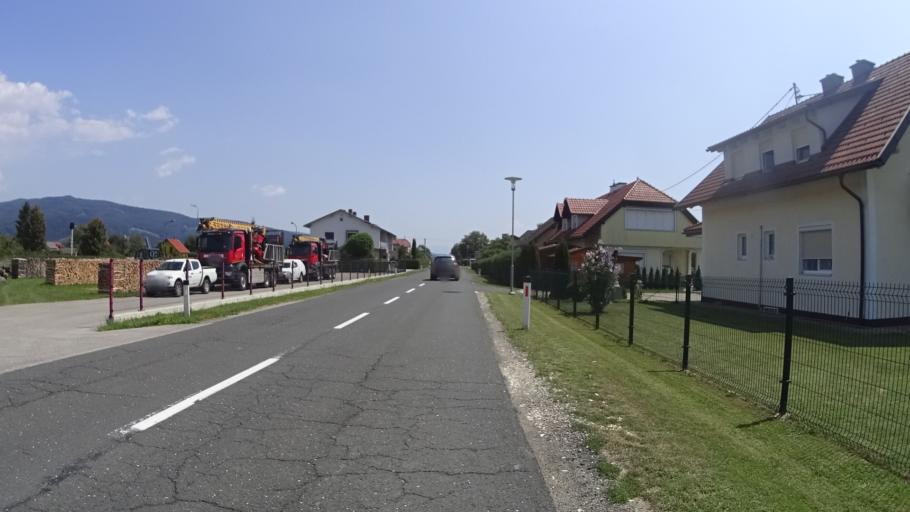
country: AT
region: Carinthia
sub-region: Politischer Bezirk Volkermarkt
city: Bleiburg/Pliberk
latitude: 46.5752
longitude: 14.7790
